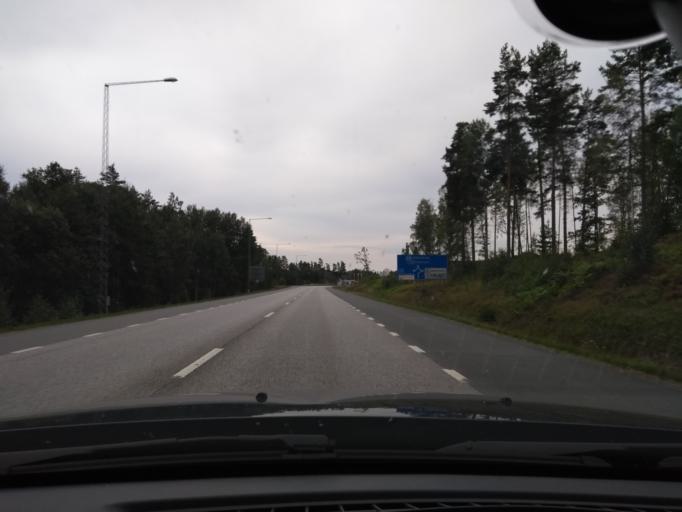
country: SE
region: Joenkoeping
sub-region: Eksjo Kommun
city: Eksjoe
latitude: 57.6526
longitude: 14.9539
